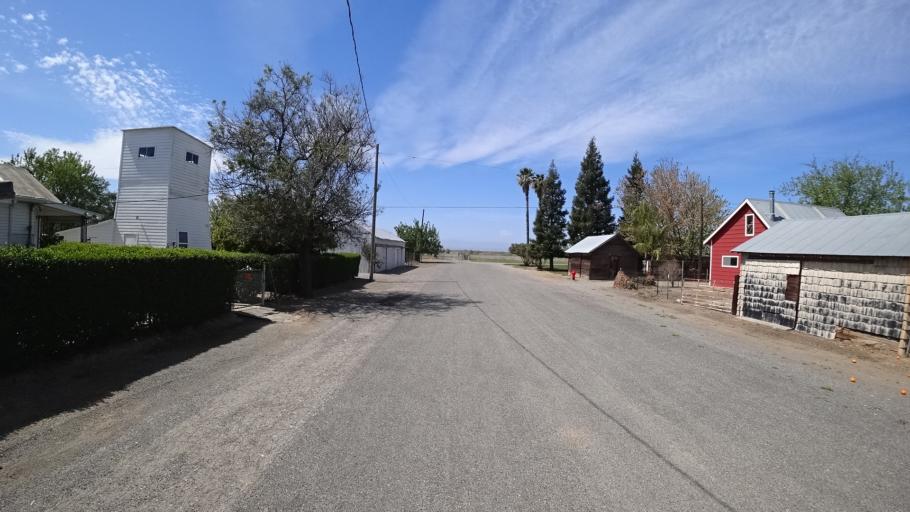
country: US
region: California
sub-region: Glenn County
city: Willows
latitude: 39.6206
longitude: -122.1958
